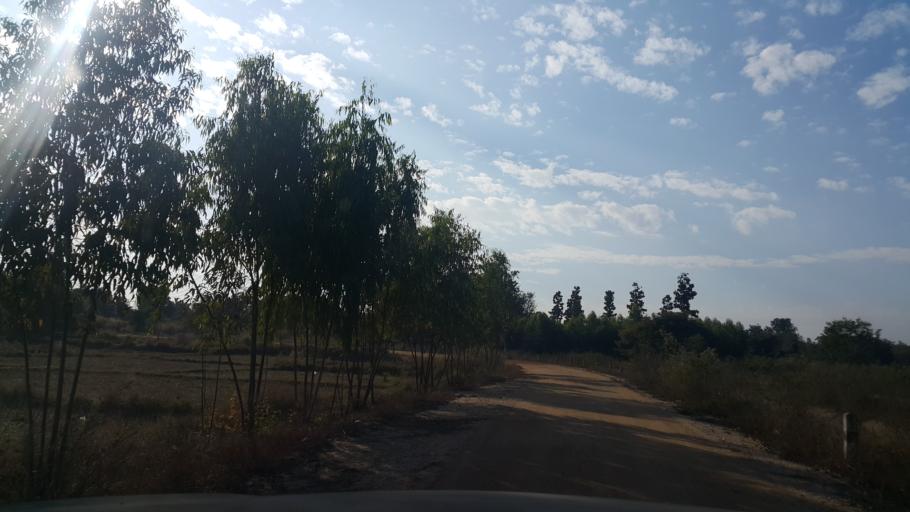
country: TH
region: Lampang
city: Ko Kha
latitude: 18.2413
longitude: 99.3600
